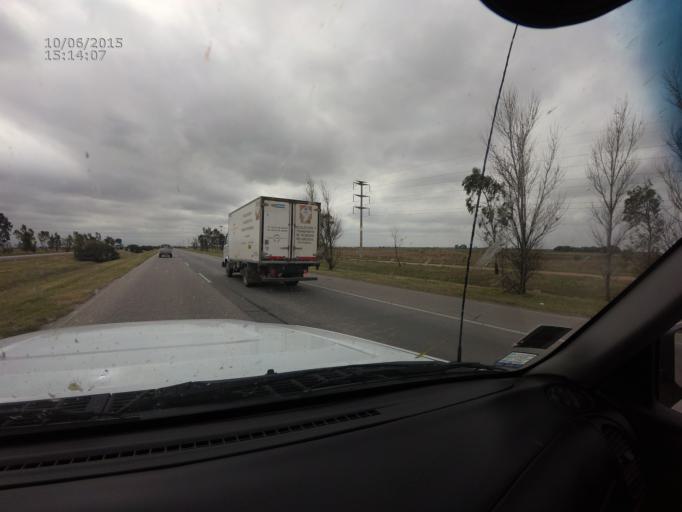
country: AR
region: Cordoba
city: Toledo
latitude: -31.5722
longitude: -63.9386
